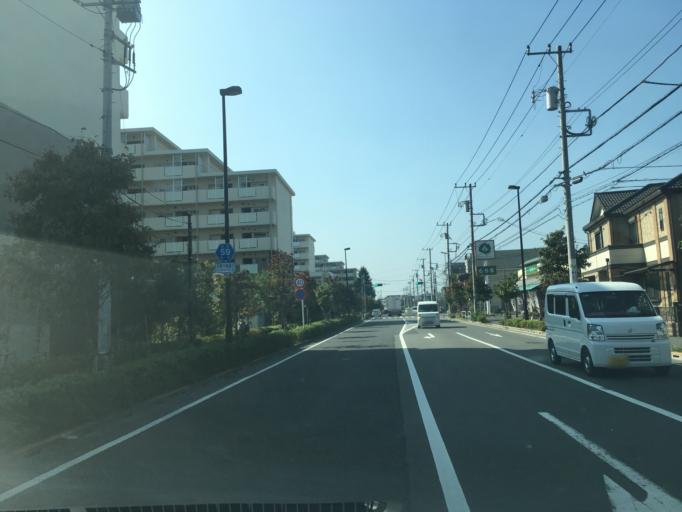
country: JP
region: Tokyo
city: Hino
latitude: 35.7130
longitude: 139.3799
